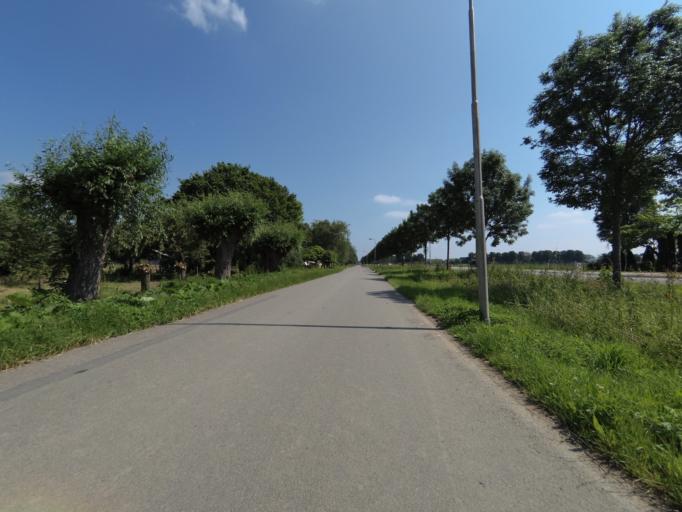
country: NL
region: Gelderland
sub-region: Gemeente Culemborg
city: Culemborg
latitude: 51.9390
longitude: 5.1879
